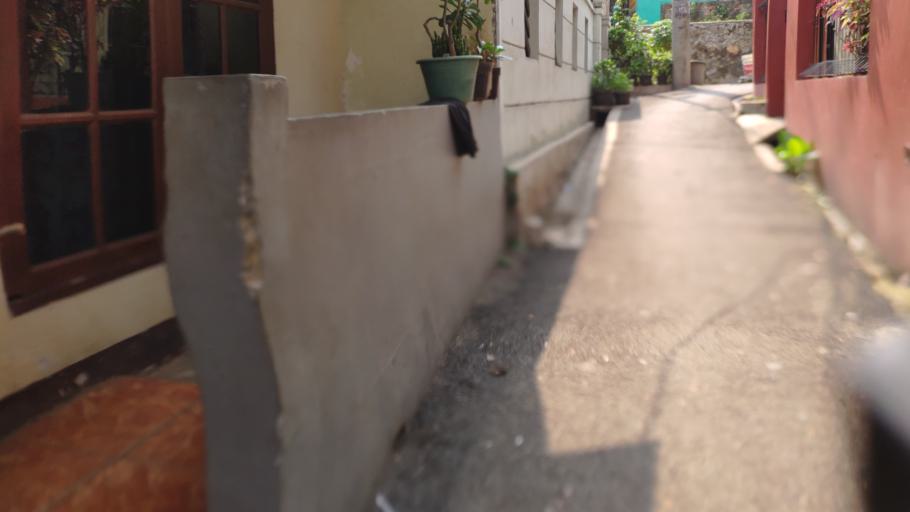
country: ID
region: West Java
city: Depok
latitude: -6.3199
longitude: 106.8161
